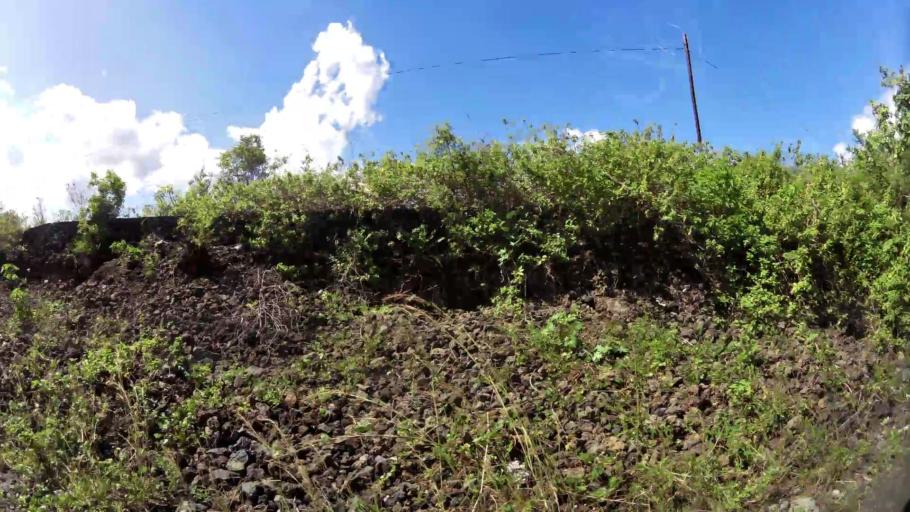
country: KM
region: Grande Comore
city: Mavingouni
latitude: -11.7273
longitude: 43.2374
